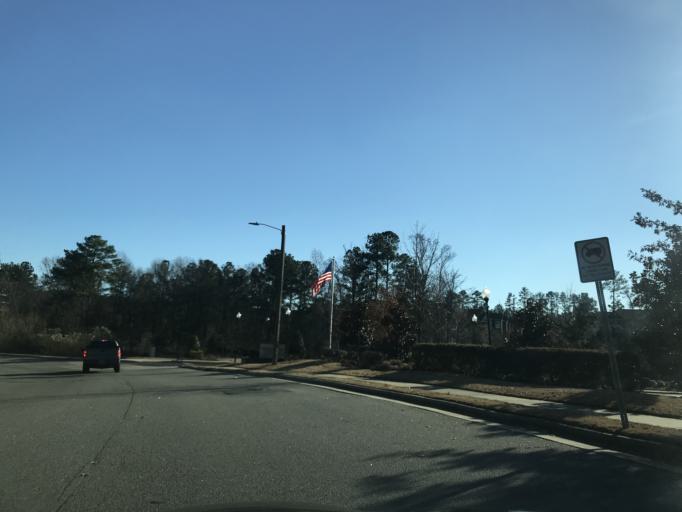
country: US
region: North Carolina
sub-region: Wake County
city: Morrisville
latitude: 35.8974
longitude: -78.8096
